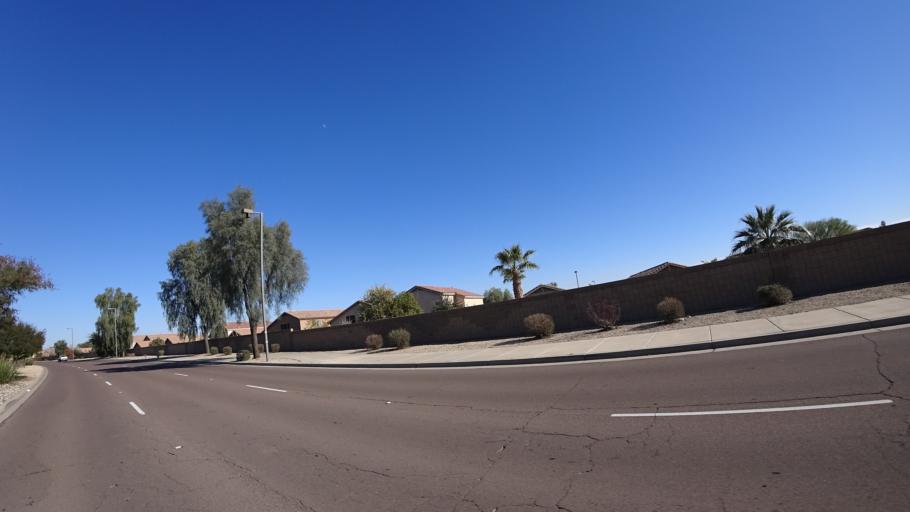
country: US
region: Arizona
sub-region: Maricopa County
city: Sun City West
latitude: 33.6494
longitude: -112.3815
